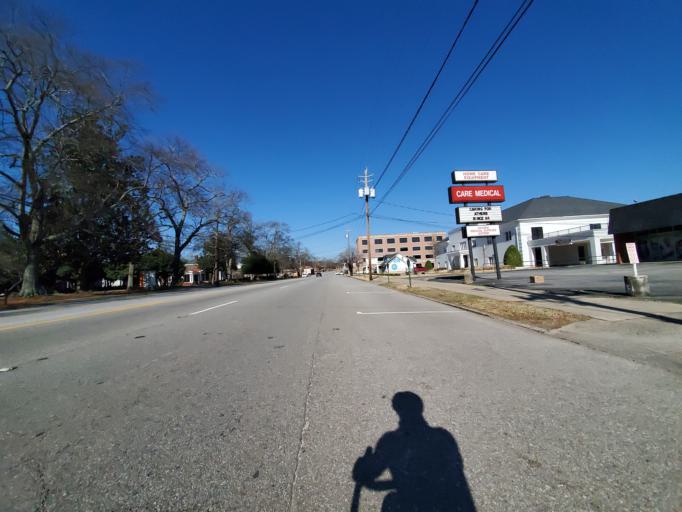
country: US
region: Georgia
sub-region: Clarke County
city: Athens
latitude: 33.9627
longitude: -83.3990
